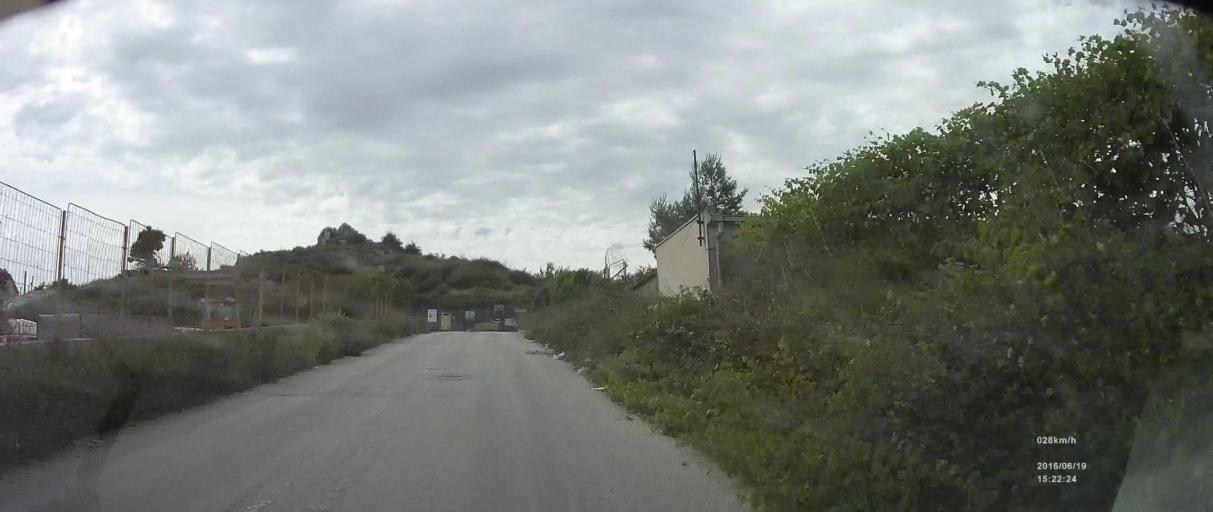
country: HR
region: Splitsko-Dalmatinska
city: Kamen
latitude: 43.5109
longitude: 16.5015
